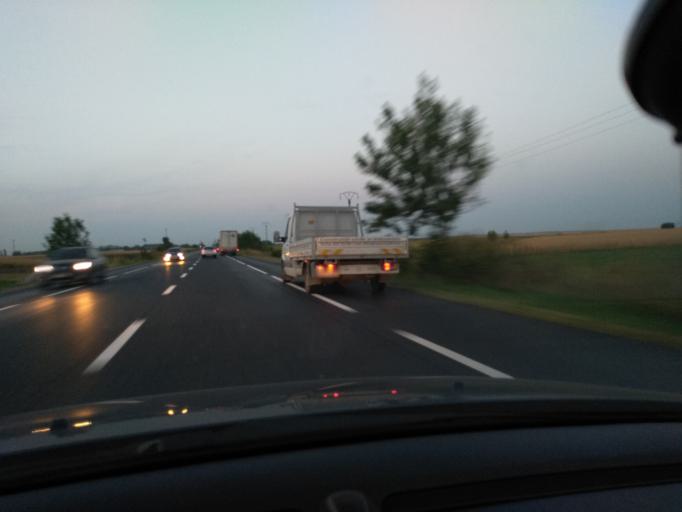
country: RO
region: Buzau
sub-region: Comuna Movila Banului
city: Limpezis
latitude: 44.9766
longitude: 26.7126
